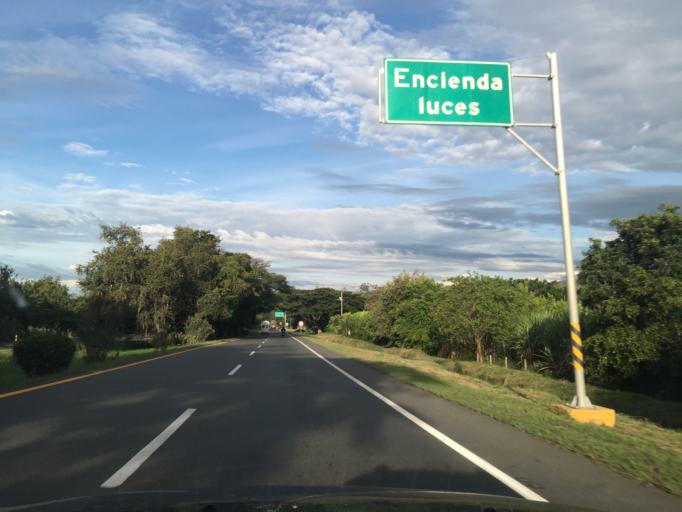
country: CO
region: Valle del Cauca
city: Bugalagrande
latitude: 4.2255
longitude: -76.1418
